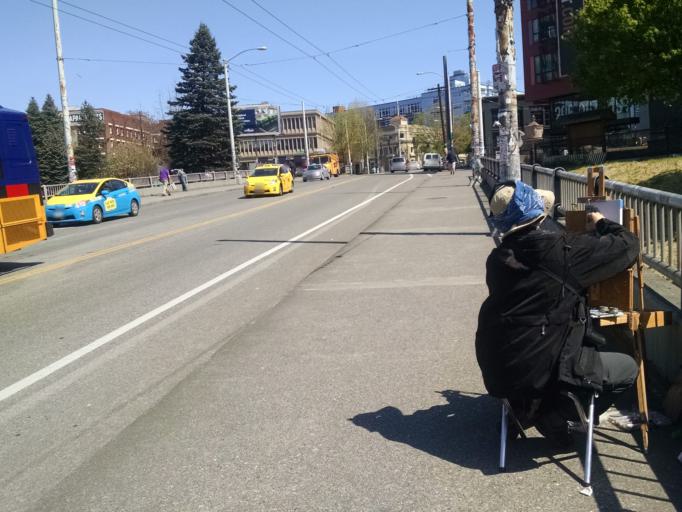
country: US
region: Washington
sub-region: King County
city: Seattle
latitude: 47.6146
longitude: -122.3294
